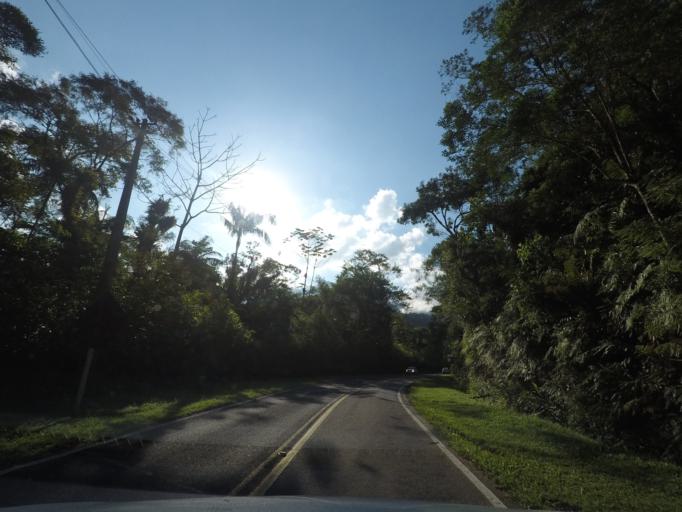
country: BR
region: Parana
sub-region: Antonina
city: Antonina
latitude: -25.4061
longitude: -48.8754
